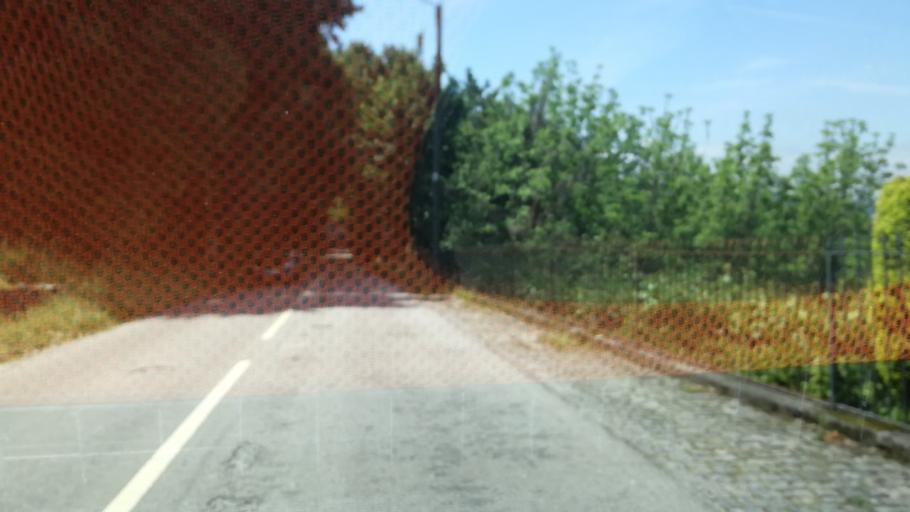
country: PT
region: Braga
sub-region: Braga
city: Adaufe
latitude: 41.5566
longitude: -8.3785
